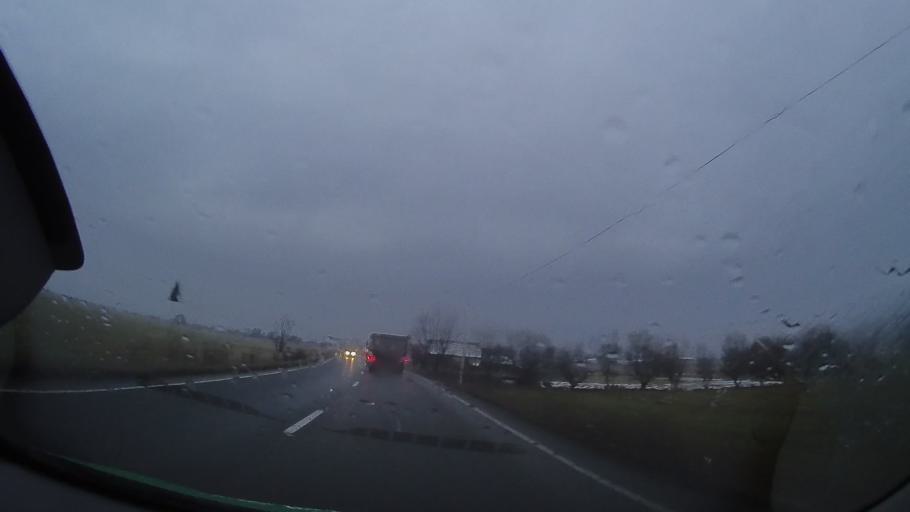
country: RO
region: Harghita
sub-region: Comuna Lazarea
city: Lazarea
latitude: 46.7599
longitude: 25.5162
